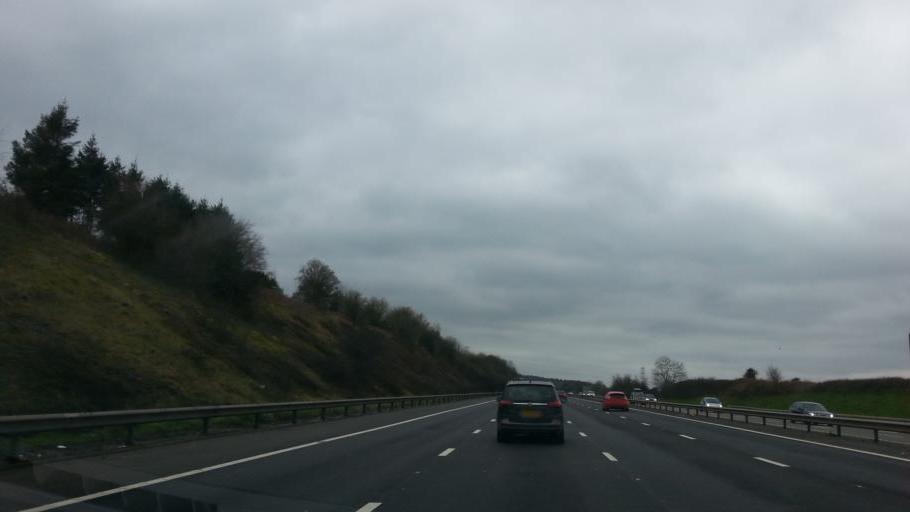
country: GB
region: England
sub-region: North Somerset
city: Portishead
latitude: 51.4683
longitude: -2.7413
